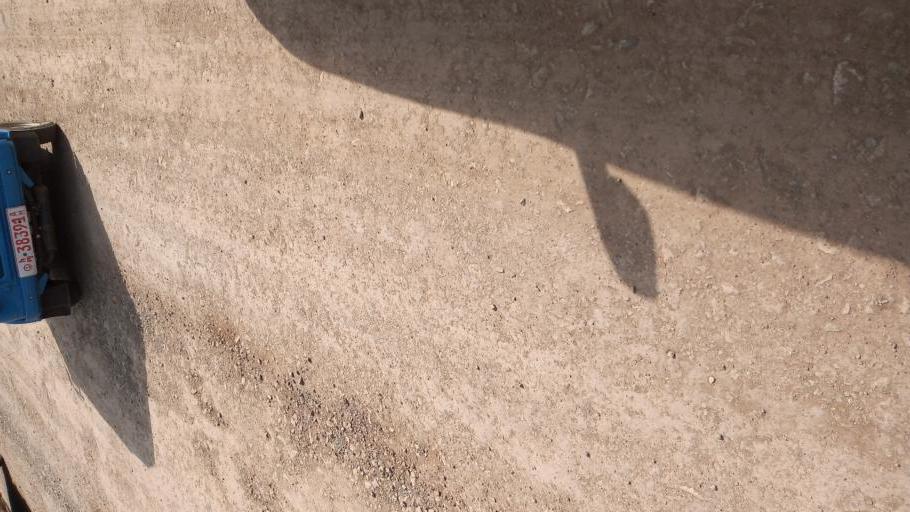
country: ET
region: Amhara
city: Gondar
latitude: 12.5750
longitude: 37.4326
